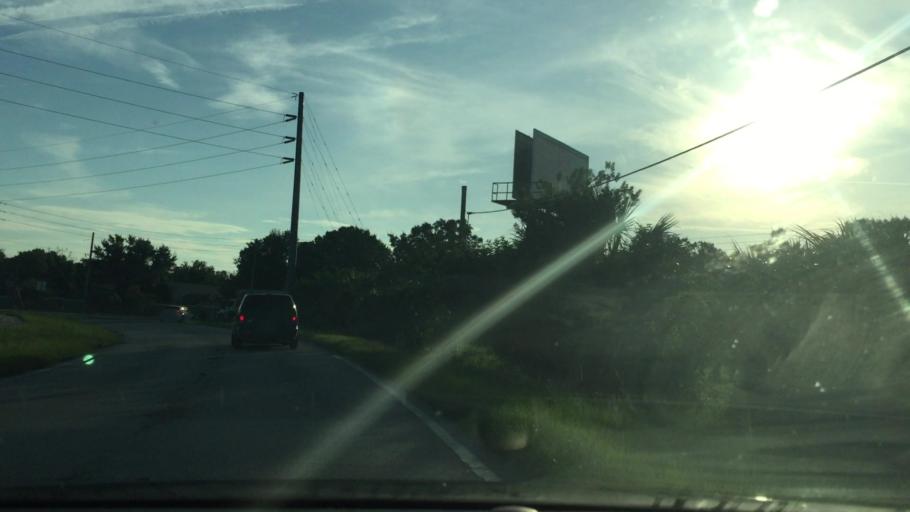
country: US
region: Florida
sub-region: Orange County
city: Pine Hills
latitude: 28.5557
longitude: -81.4314
